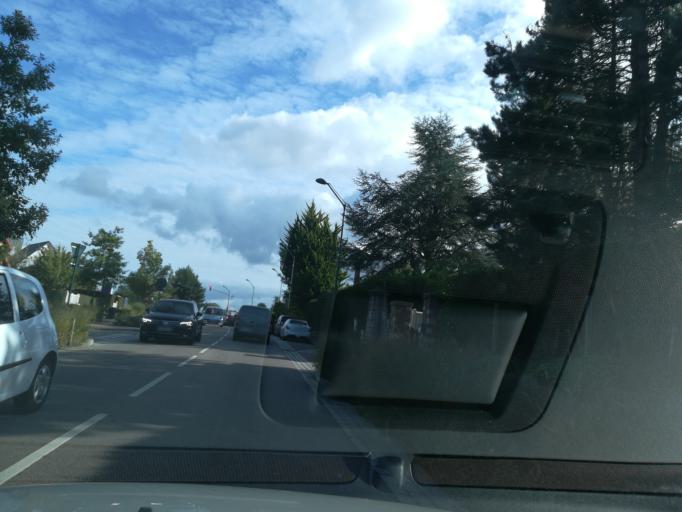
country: FR
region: Haute-Normandie
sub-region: Departement de la Seine-Maritime
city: Bois-Guillaume
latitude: 49.4715
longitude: 1.1140
